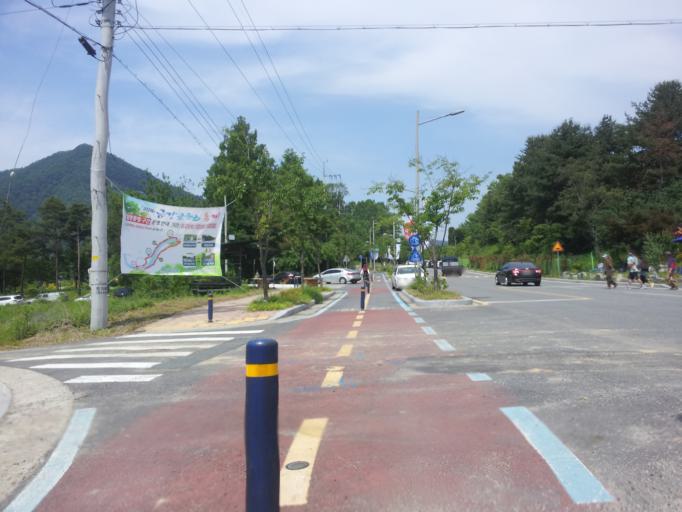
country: KR
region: Daejeon
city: Sintansin
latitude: 36.4700
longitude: 127.4719
